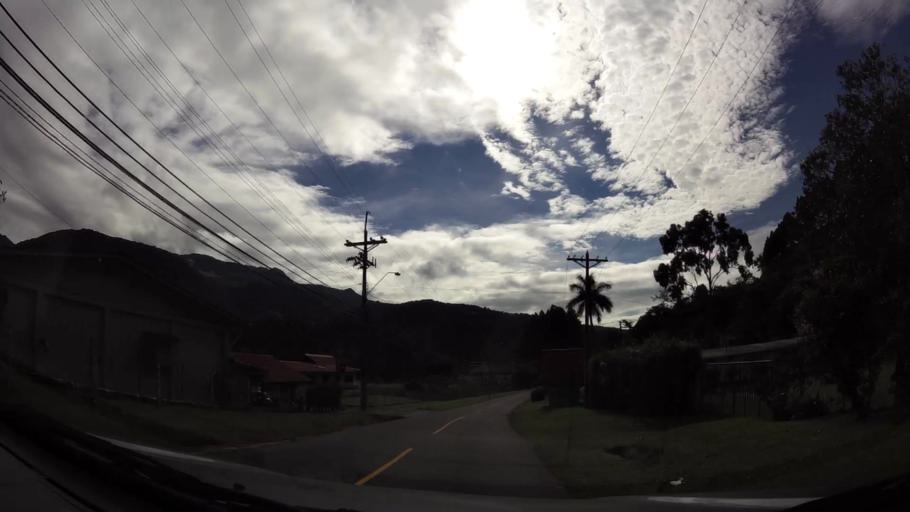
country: PA
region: Chiriqui
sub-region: Distrito Boquete
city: Boquete
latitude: 8.7870
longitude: -82.4366
